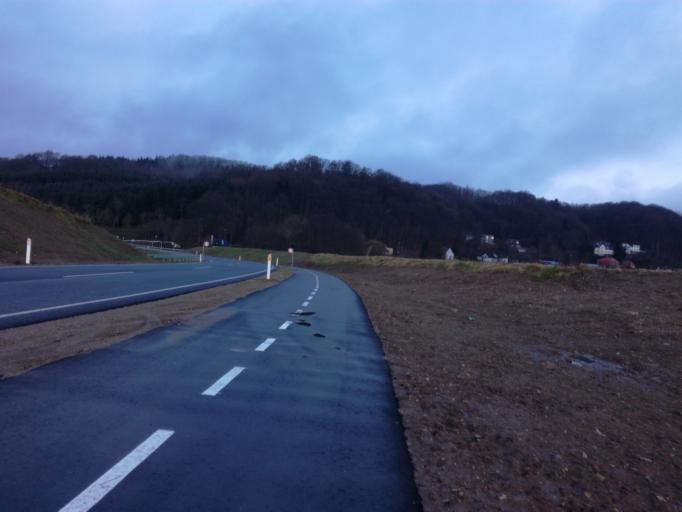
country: DK
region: South Denmark
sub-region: Vejle Kommune
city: Vejle
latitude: 55.7109
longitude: 9.4971
